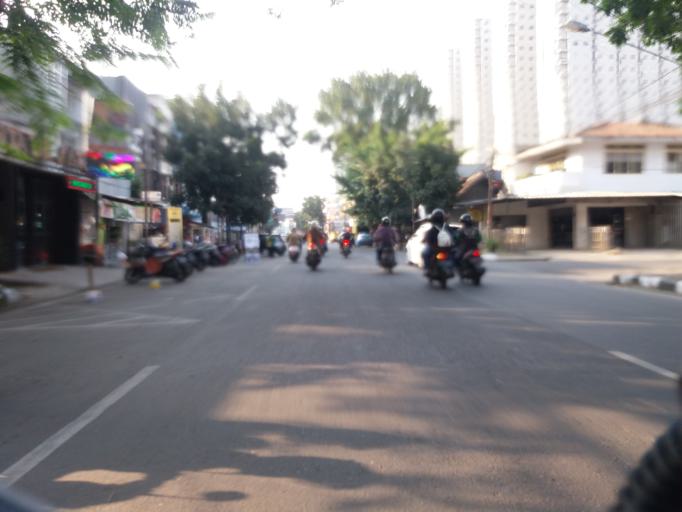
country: ID
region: West Java
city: Bandung
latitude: -6.9253
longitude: 107.6173
